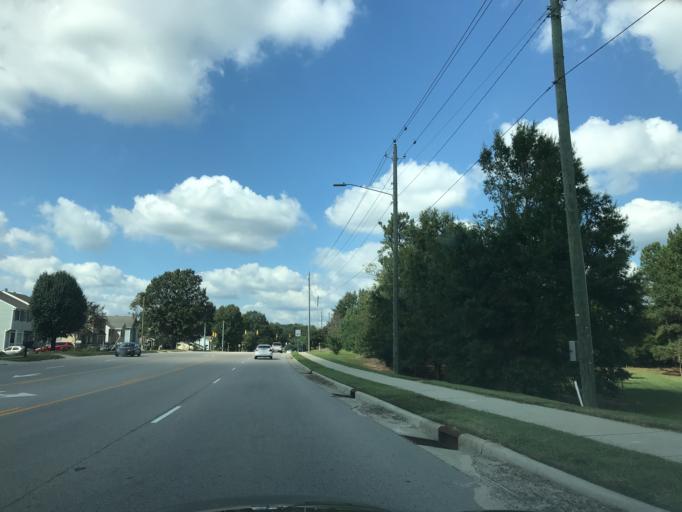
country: US
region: North Carolina
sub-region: Wake County
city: Rolesville
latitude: 35.8847
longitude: -78.5526
